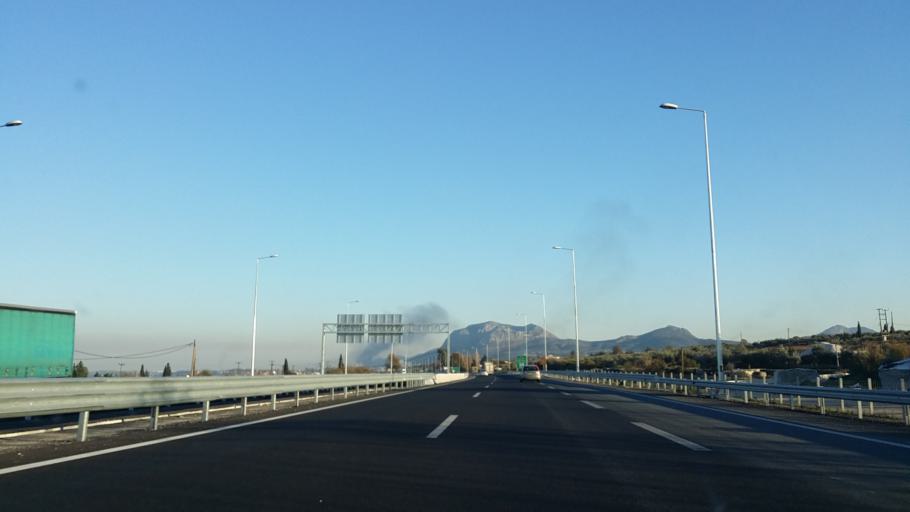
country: GR
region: Peloponnese
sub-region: Nomos Korinthias
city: Zevgolateio
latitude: 37.9271
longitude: 22.7930
